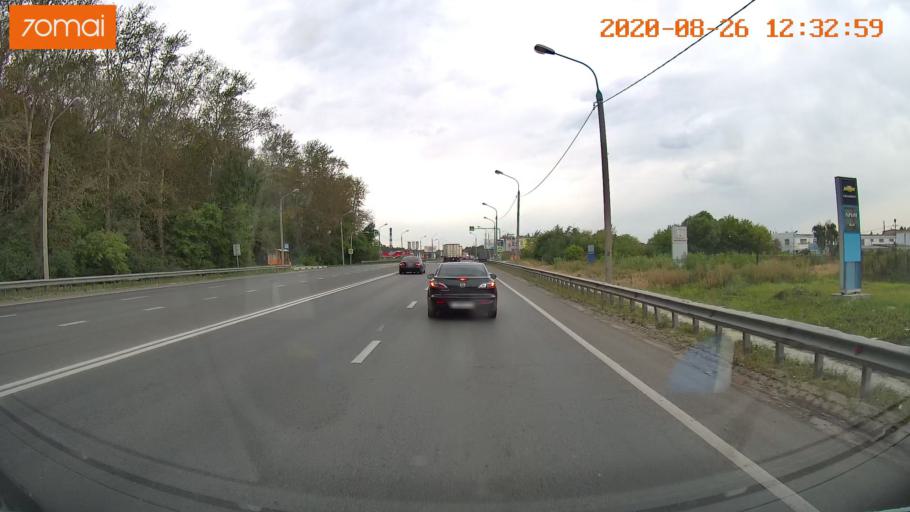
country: RU
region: Rjazan
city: Ryazan'
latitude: 54.5801
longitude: 39.7817
